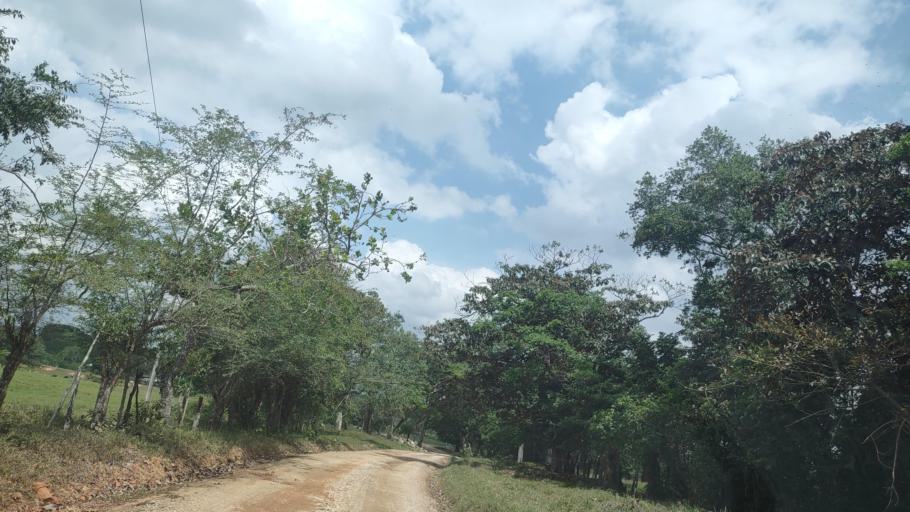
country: MX
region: Veracruz
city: Las Choapas
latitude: 17.9590
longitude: -94.1173
